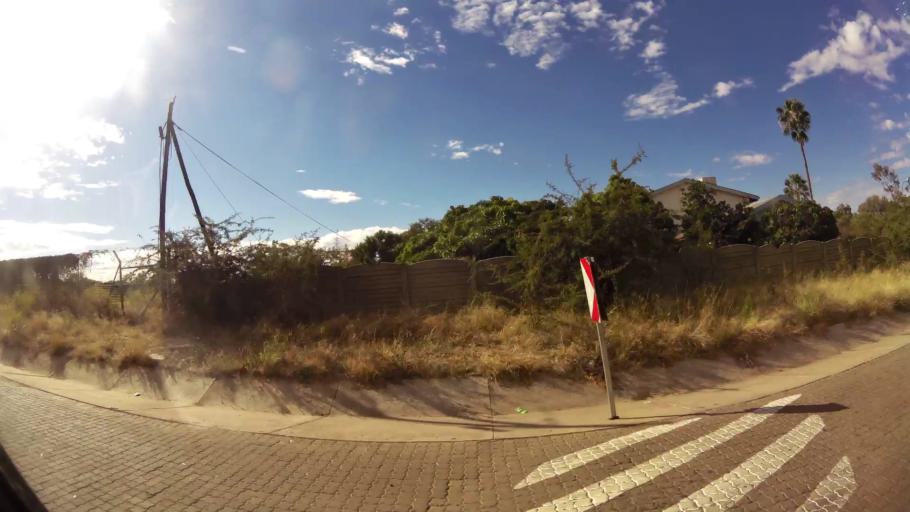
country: ZA
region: Limpopo
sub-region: Waterberg District Municipality
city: Warmbaths
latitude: -24.8792
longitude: 28.2731
